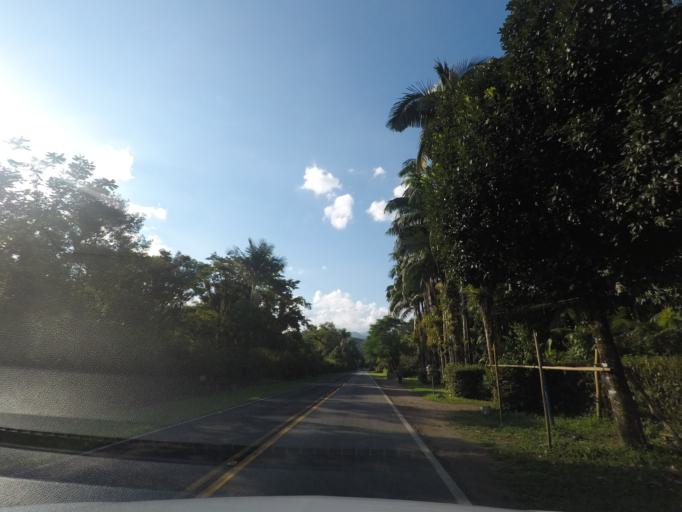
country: BR
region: Parana
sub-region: Antonina
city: Antonina
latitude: -25.4023
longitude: -48.8725
